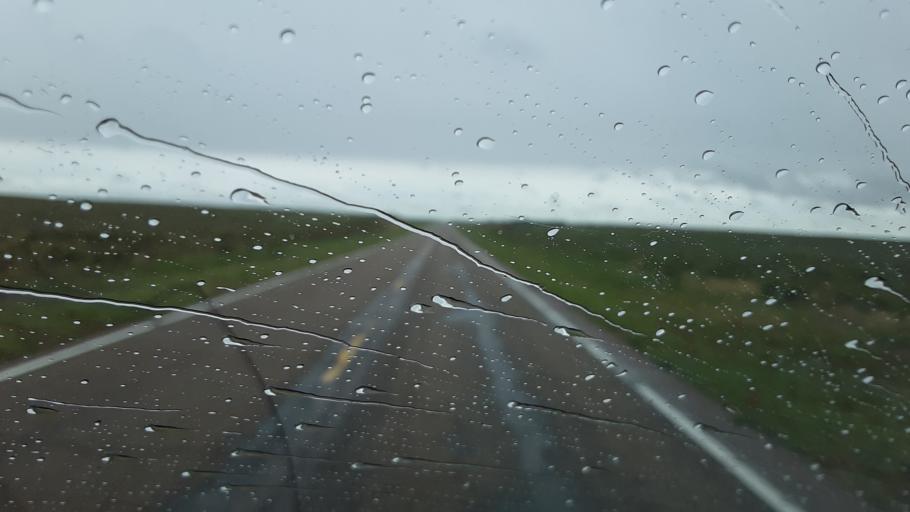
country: US
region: Colorado
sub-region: Lincoln County
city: Hugo
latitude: 38.8495
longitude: -103.2250
